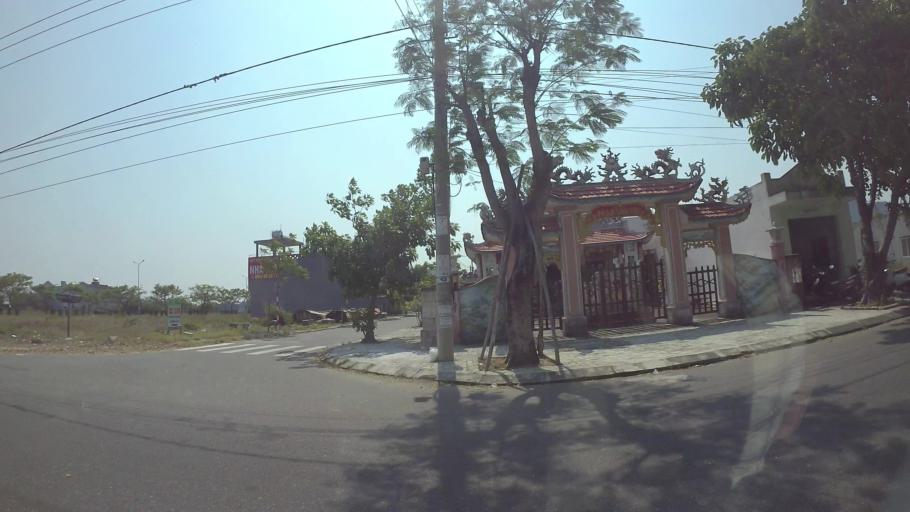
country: VN
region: Da Nang
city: Ngu Hanh Son
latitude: 15.9863
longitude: 108.2699
